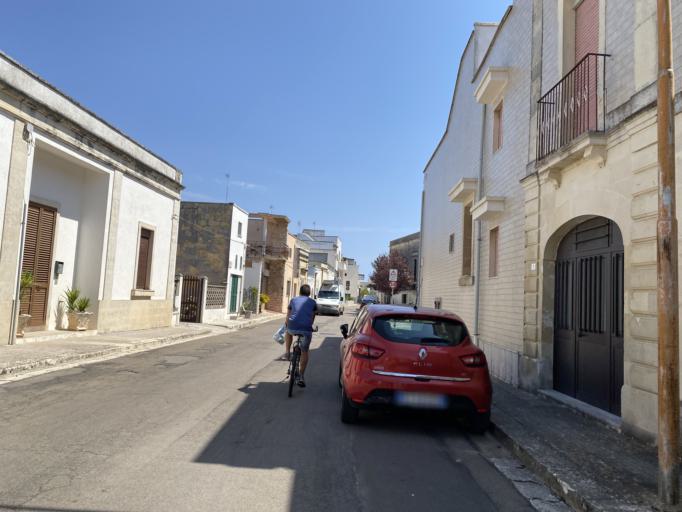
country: IT
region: Apulia
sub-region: Provincia di Lecce
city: Giuggianello
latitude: 40.0950
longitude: 18.3672
